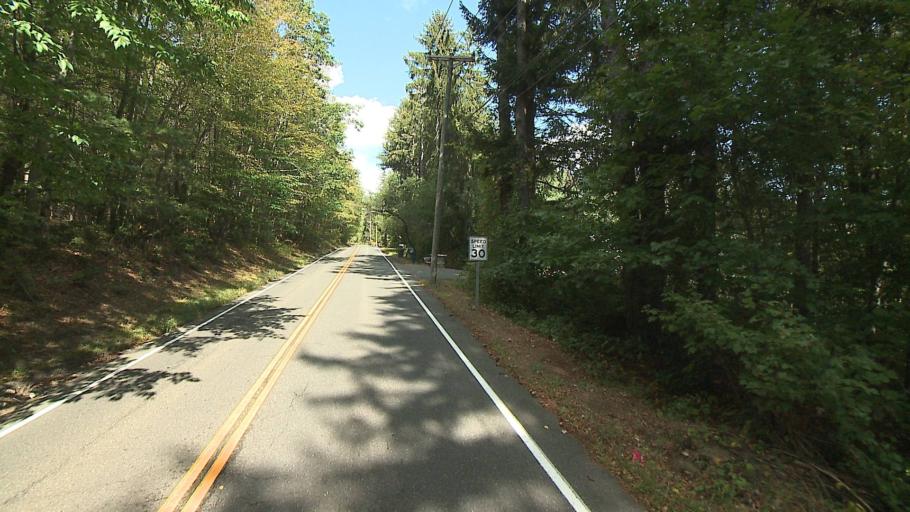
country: US
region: Connecticut
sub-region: New Haven County
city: Oxford
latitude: 41.4335
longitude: -73.0863
